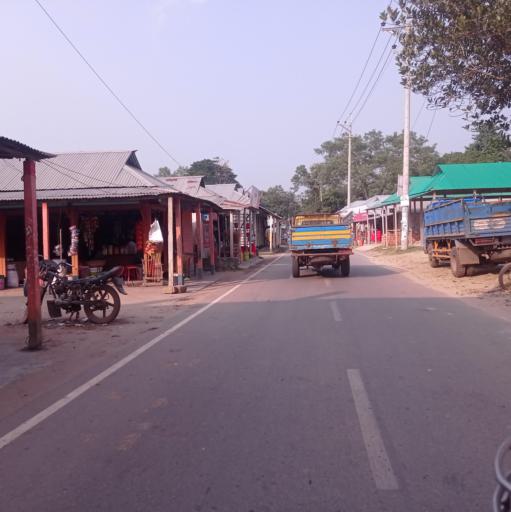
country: BD
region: Dhaka
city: Bhairab Bazar
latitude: 24.0813
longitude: 90.8491
